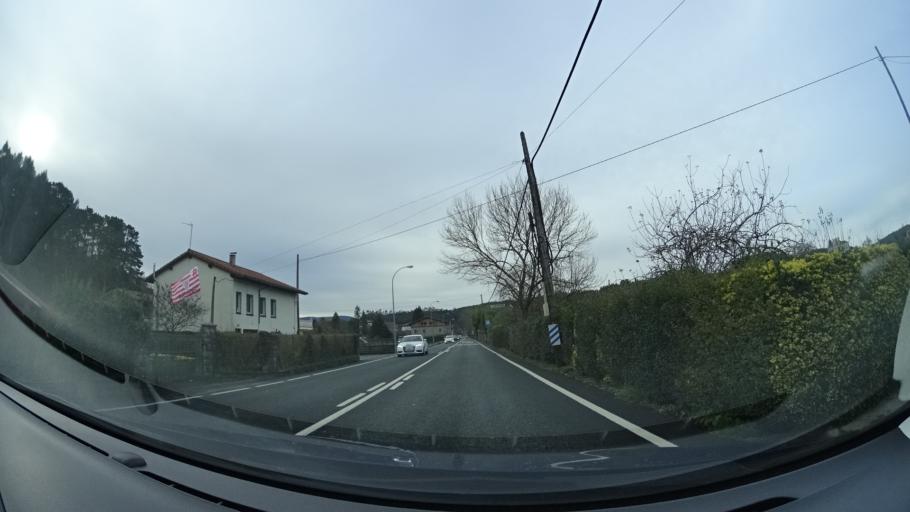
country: ES
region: Basque Country
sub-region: Bizkaia
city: Mungia
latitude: 43.3692
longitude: -2.8078
